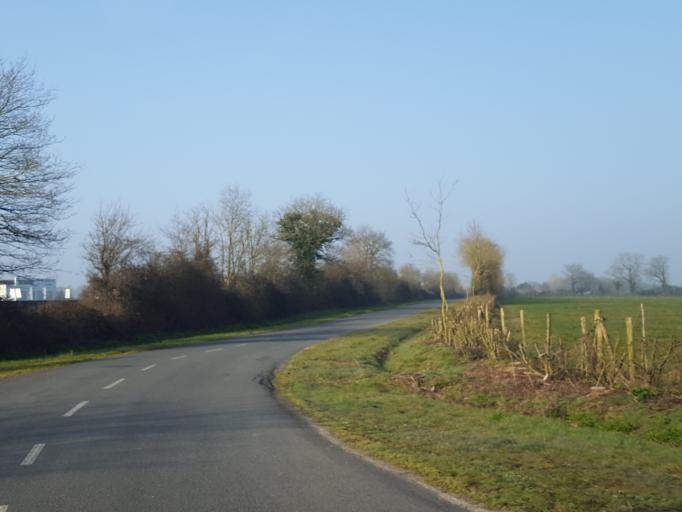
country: FR
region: Pays de la Loire
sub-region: Departement de la Vendee
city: La Chaize-le-Vicomte
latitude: 46.6696
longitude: -1.3220
